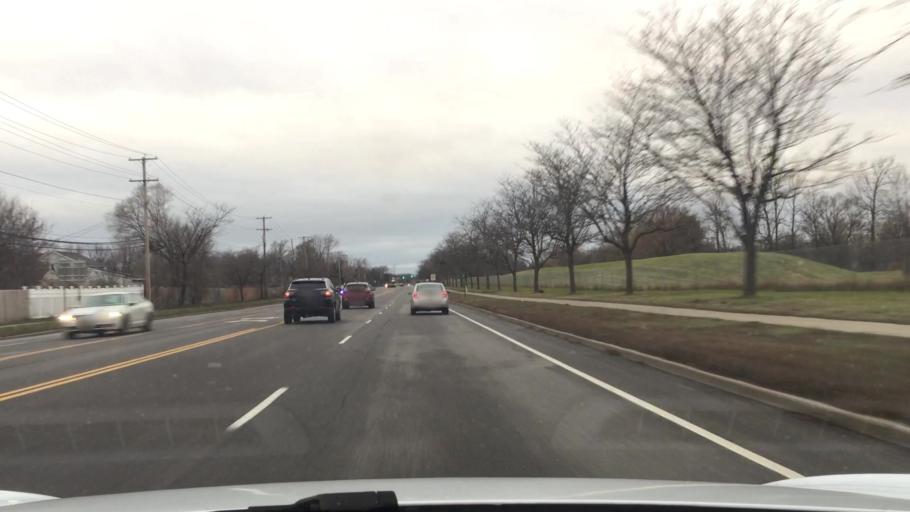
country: US
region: New York
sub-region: Erie County
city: Amherst
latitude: 42.9782
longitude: -78.7696
